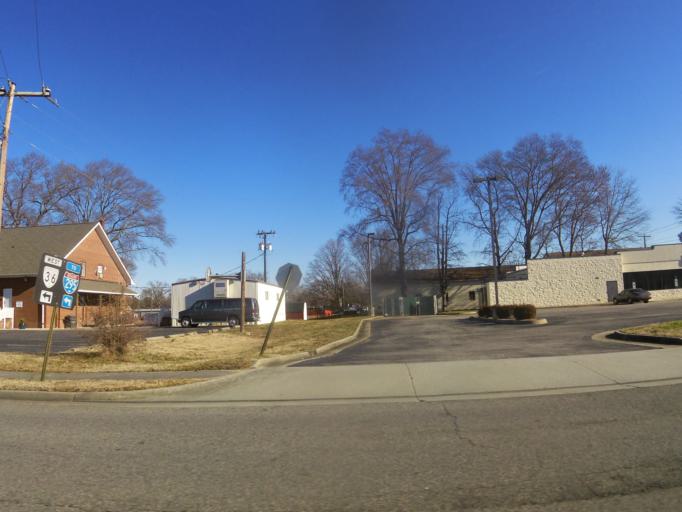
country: US
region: Virginia
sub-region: Prince George County
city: Fort Lee
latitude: 37.2727
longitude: -77.3155
